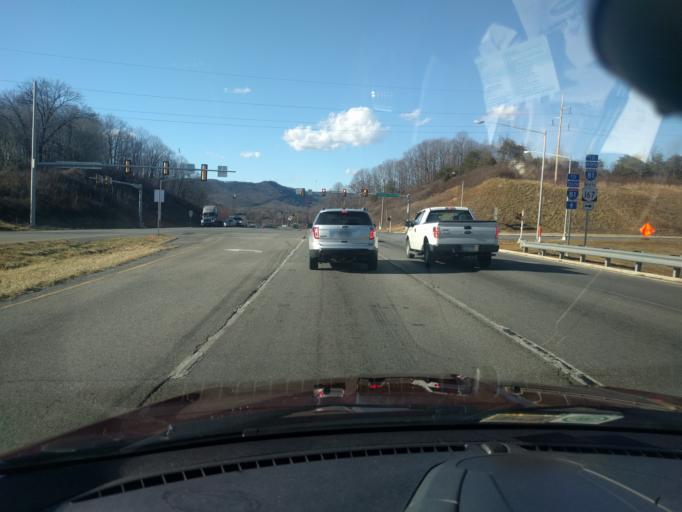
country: US
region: Virginia
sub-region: Botetourt County
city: Cloverdale
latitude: 37.3846
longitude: -79.8971
